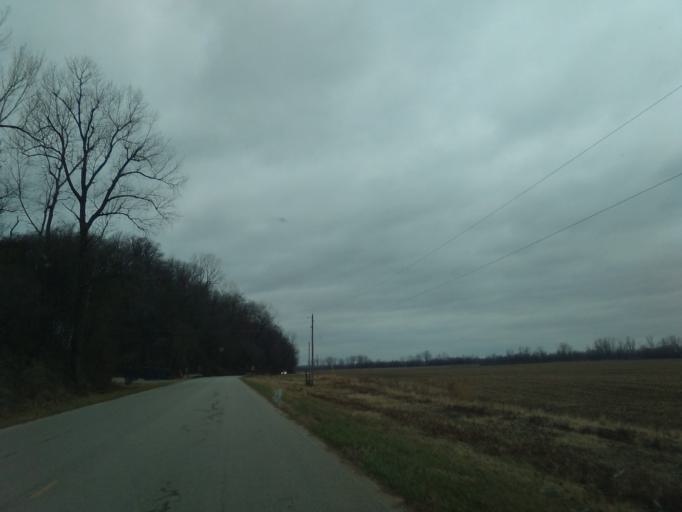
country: US
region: Missouri
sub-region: Holt County
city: Mound City
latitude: 40.0245
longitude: -95.3576
